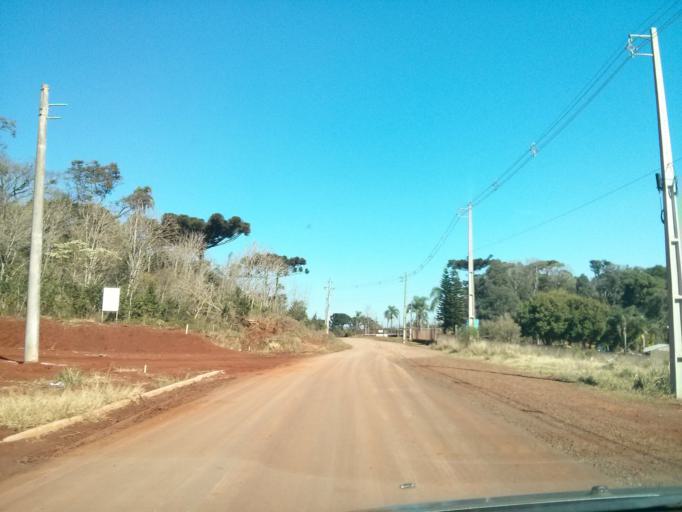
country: BR
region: Santa Catarina
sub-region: Chapeco
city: Chapeco
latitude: -27.0900
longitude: -52.6930
